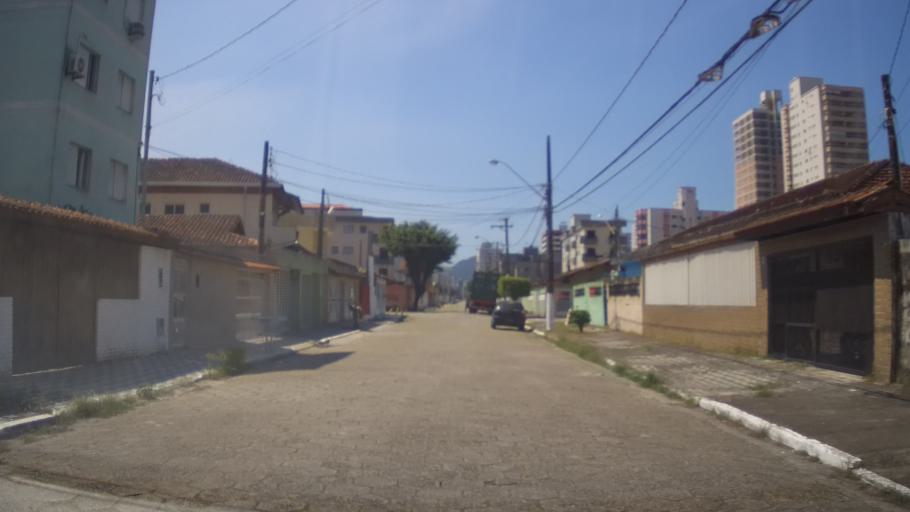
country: BR
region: Sao Paulo
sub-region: Praia Grande
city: Praia Grande
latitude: -24.0164
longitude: -46.4477
